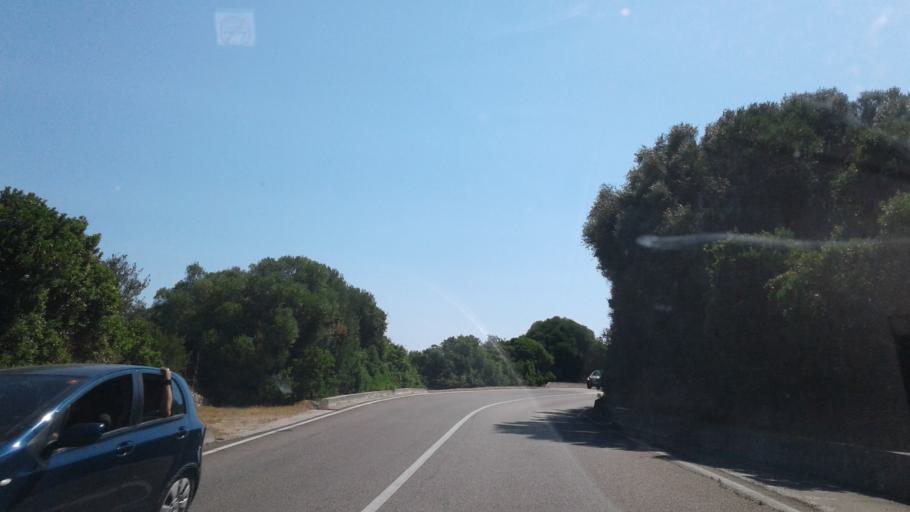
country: IT
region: Sardinia
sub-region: Provincia di Olbia-Tempio
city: Palau
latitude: 41.1693
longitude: 9.3282
